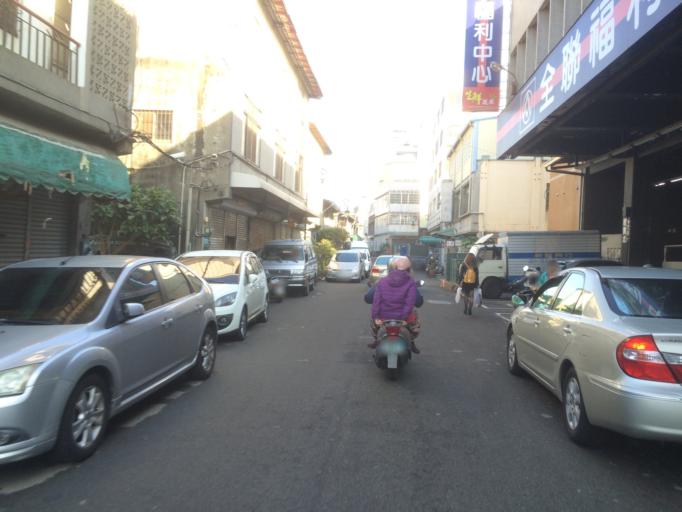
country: TW
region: Taiwan
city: Fengyuan
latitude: 24.2119
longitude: 120.7063
